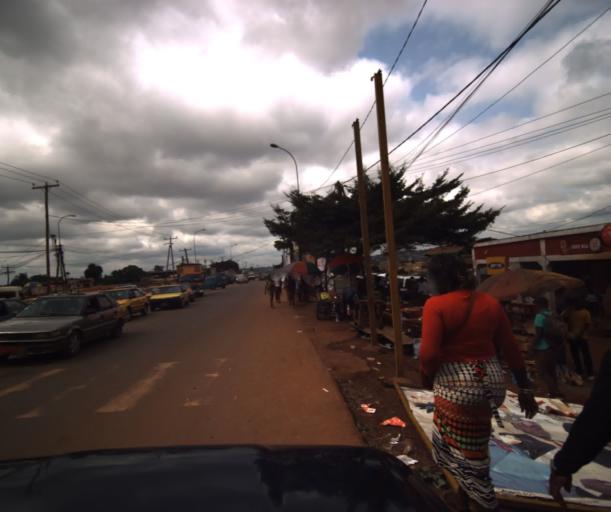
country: CM
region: Centre
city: Yaounde
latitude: 3.8256
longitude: 11.5169
